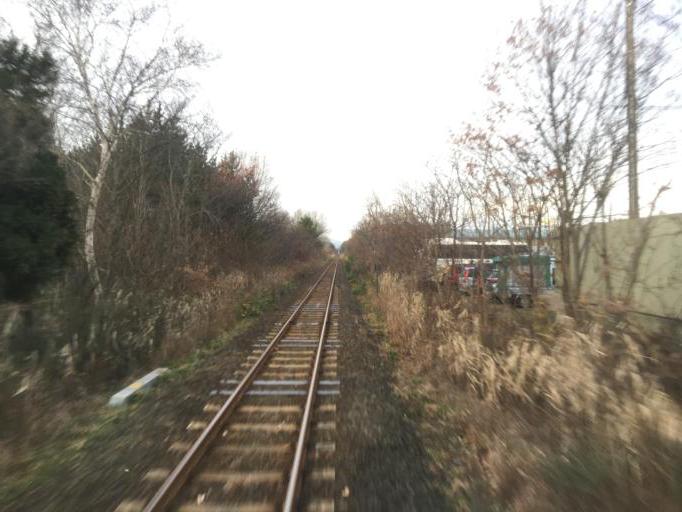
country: JP
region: Aomori
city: Mutsu
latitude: 41.2594
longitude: 141.2203
